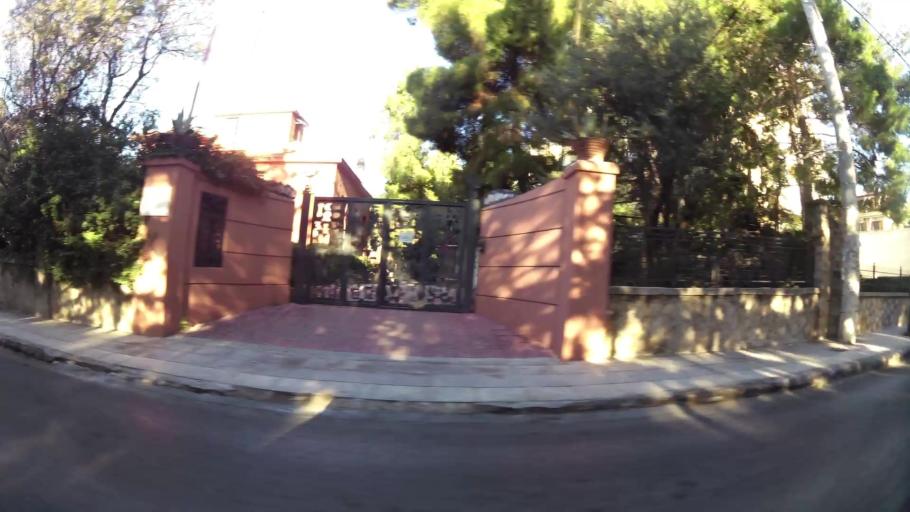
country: GR
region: Attica
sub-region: Nomarchia Athinas
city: Lykovrysi
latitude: 38.0636
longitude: 23.7756
